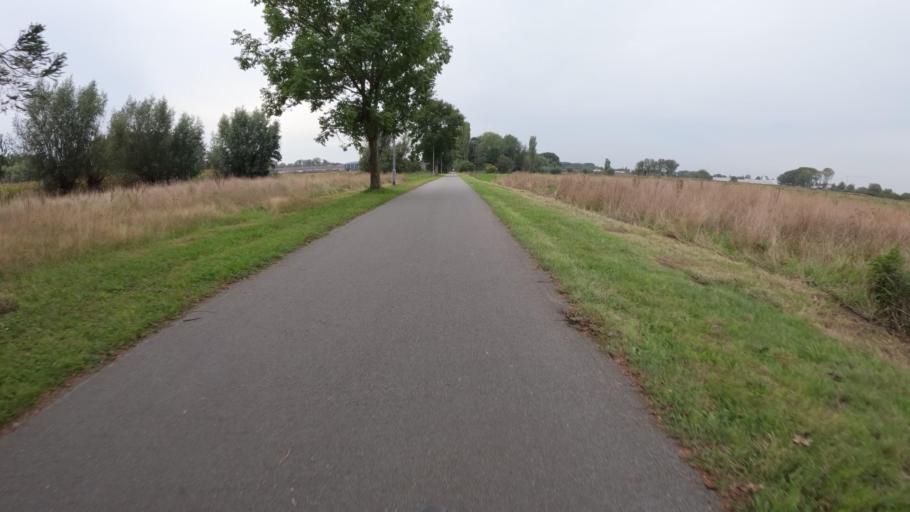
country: BE
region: Flanders
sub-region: Provincie Oost-Vlaanderen
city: Stekene
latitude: 51.2098
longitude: 4.0648
